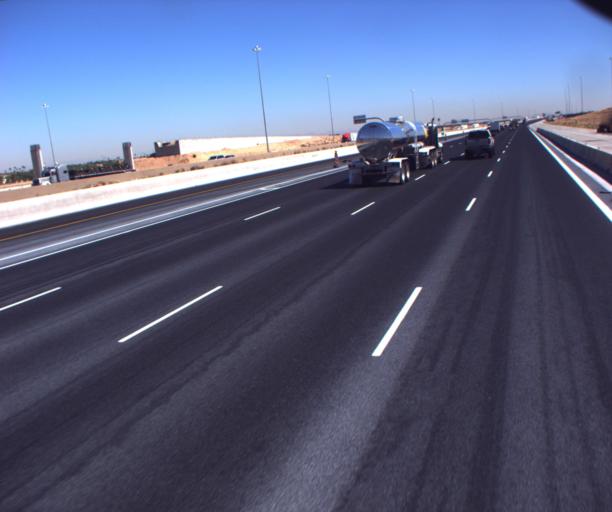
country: US
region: Arizona
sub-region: Maricopa County
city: Goodyear
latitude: 33.4616
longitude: -112.4239
